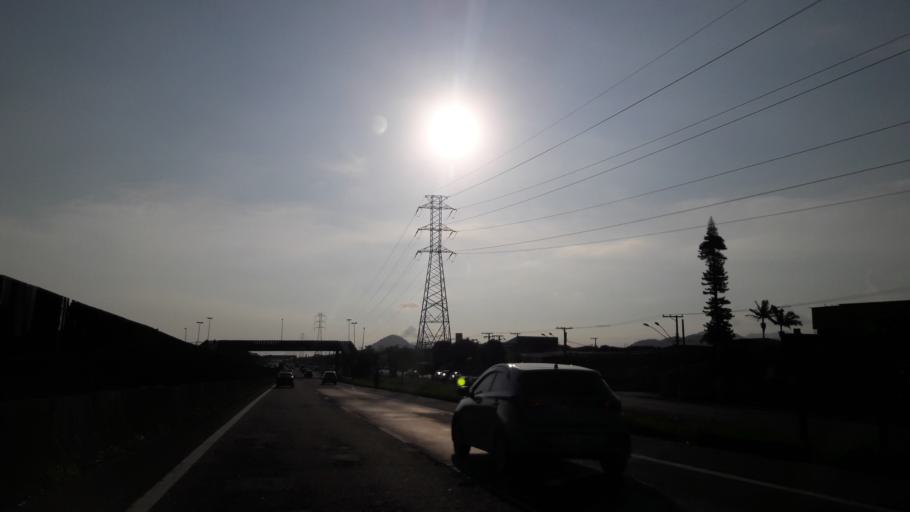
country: BR
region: Sao Paulo
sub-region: Mongagua
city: Mongagua
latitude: -24.1011
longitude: -46.6367
